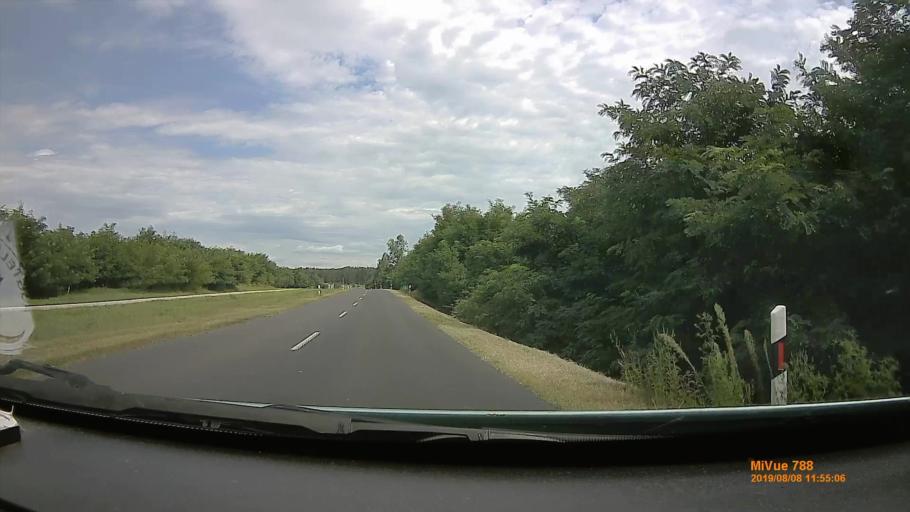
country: HU
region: Szabolcs-Szatmar-Bereg
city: Nyirmihalydi
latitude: 47.7387
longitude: 21.9760
